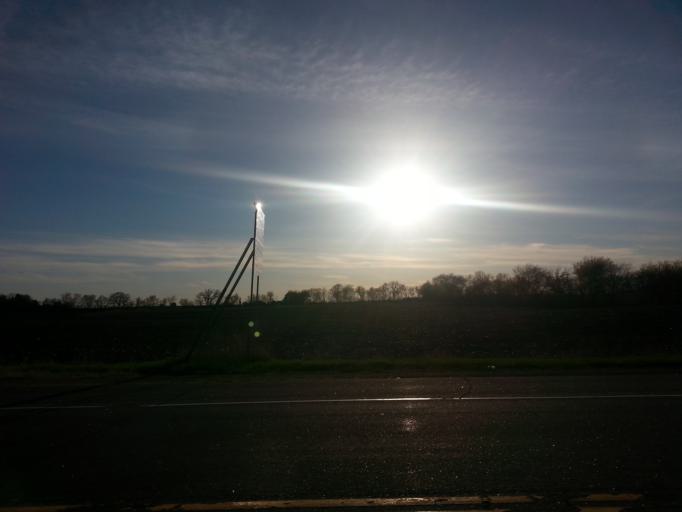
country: US
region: Wisconsin
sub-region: Pierce County
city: Prescott
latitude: 44.6036
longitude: -92.7724
